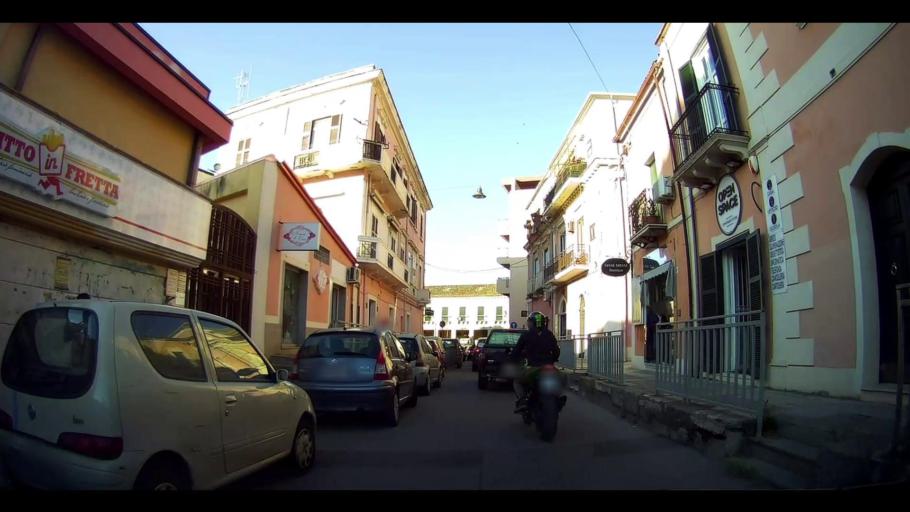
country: IT
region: Calabria
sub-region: Provincia di Crotone
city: Crotone
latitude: 39.0796
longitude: 17.1272
